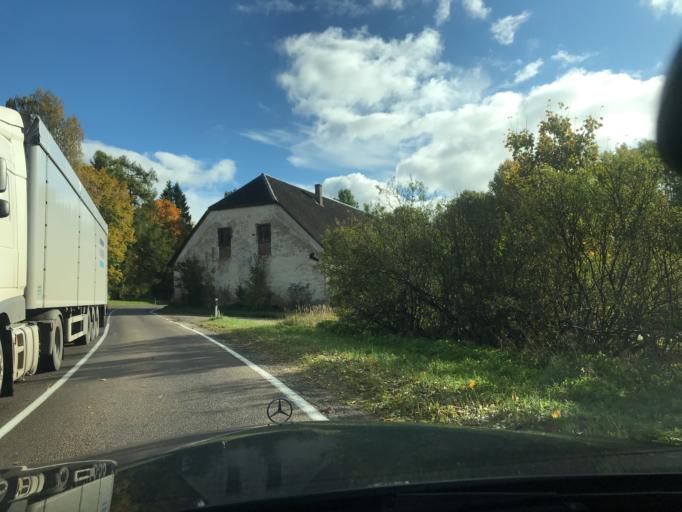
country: EE
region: Valgamaa
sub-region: Torva linn
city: Torva
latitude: 58.0088
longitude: 26.2028
